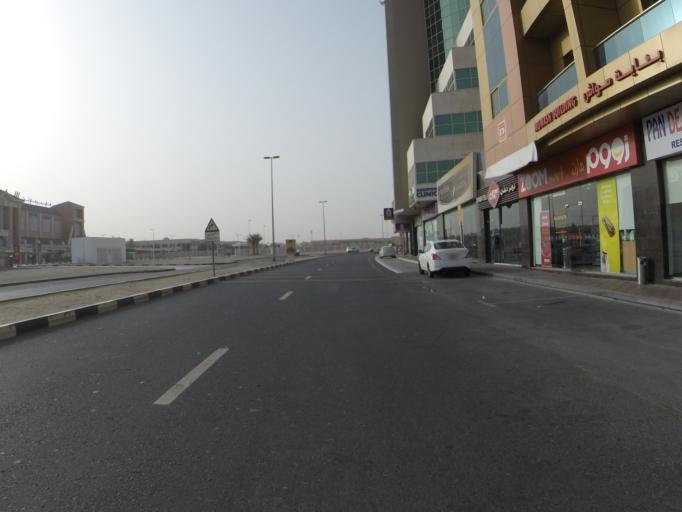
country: AE
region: Dubai
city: Dubai
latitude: 25.1169
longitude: 55.2058
